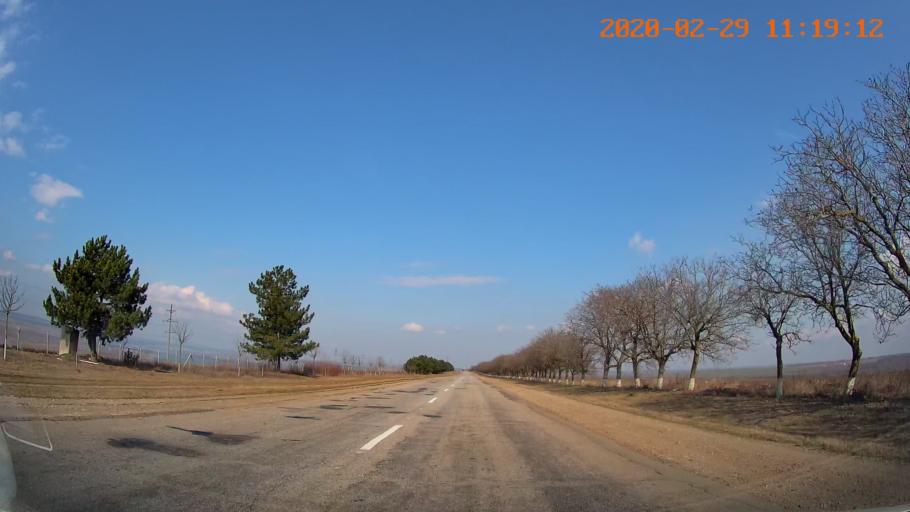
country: MD
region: Telenesti
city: Cocieri
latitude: 47.3464
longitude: 29.1754
